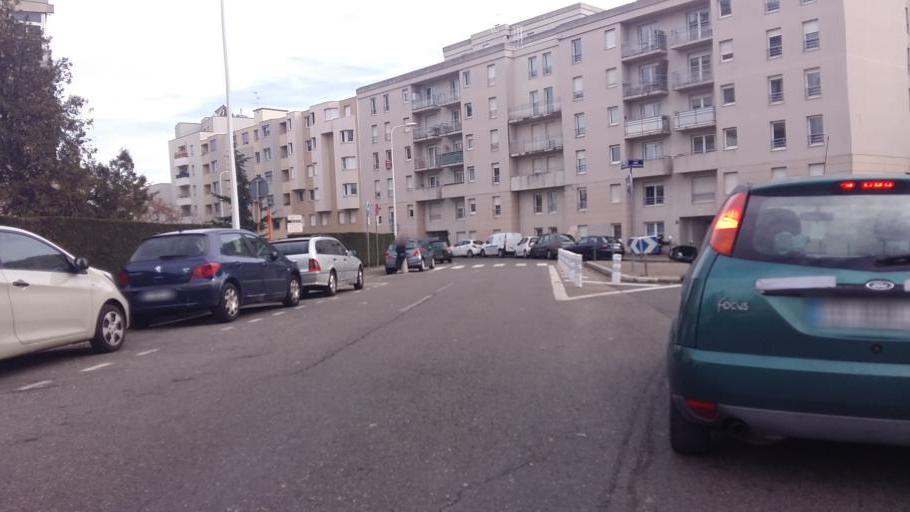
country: FR
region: Rhone-Alpes
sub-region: Departement du Rhone
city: Lyon
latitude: 45.7320
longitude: 4.8515
